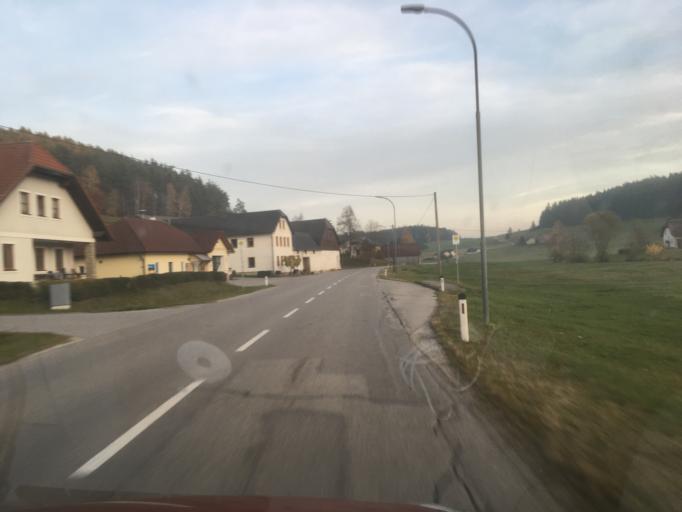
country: AT
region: Lower Austria
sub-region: Politischer Bezirk Zwettl
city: Langschlag
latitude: 48.5808
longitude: 14.8506
